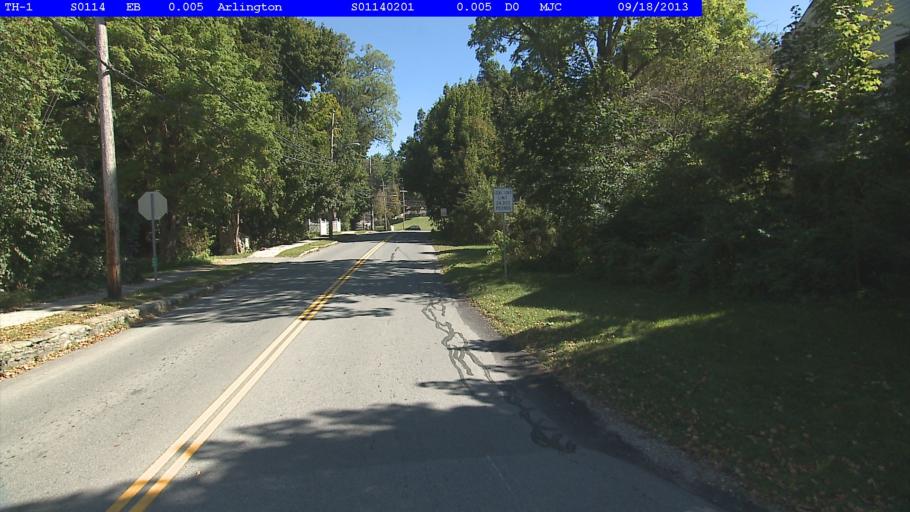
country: US
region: Vermont
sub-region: Bennington County
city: Arlington
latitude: 43.0725
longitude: -73.1548
